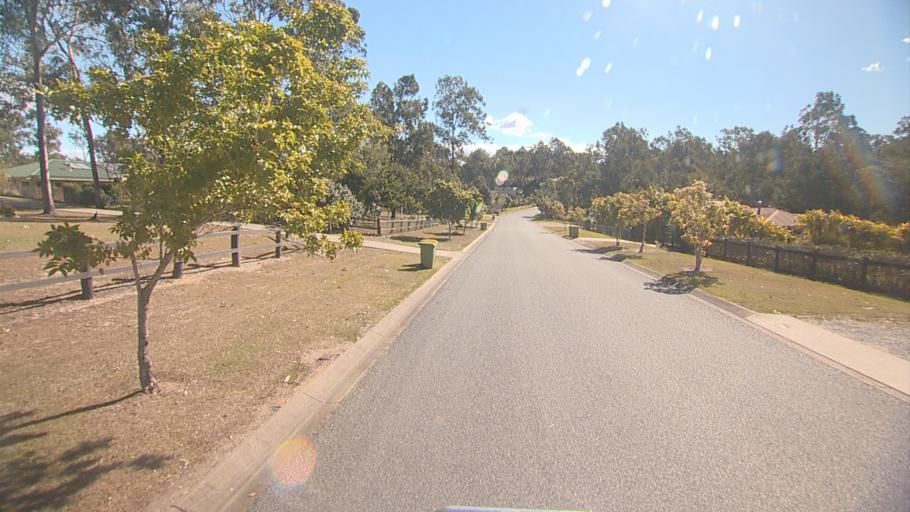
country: AU
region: Queensland
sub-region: Ipswich
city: Springfield Lakes
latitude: -27.7261
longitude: 152.9213
